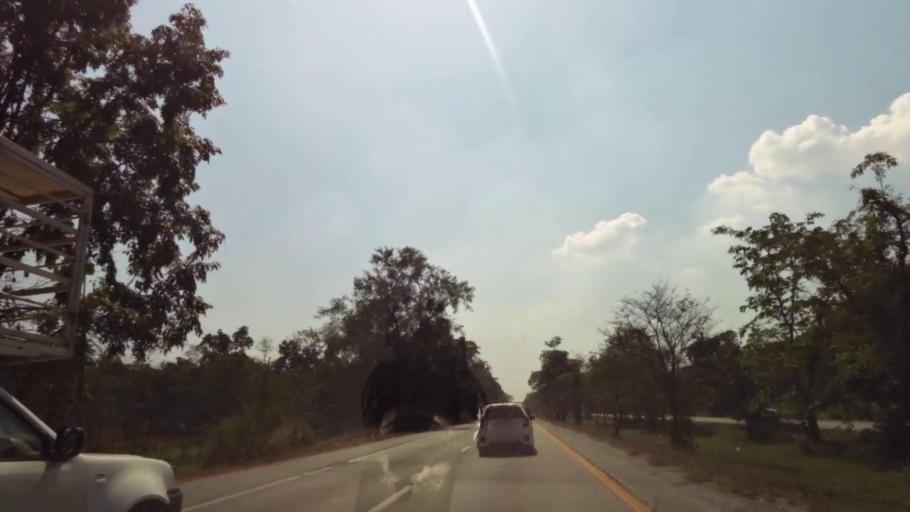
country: TH
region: Phichit
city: Wachira Barami
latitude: 16.5537
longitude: 100.1471
